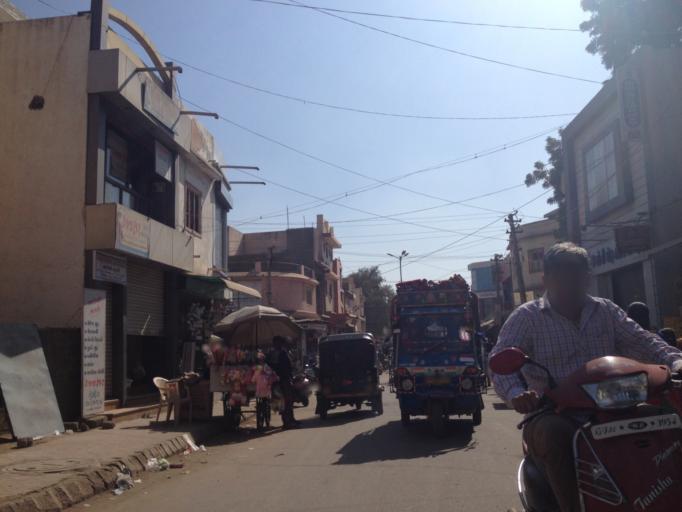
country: IN
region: Gujarat
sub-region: Kachchh
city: Anjar
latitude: 23.1136
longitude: 70.0279
